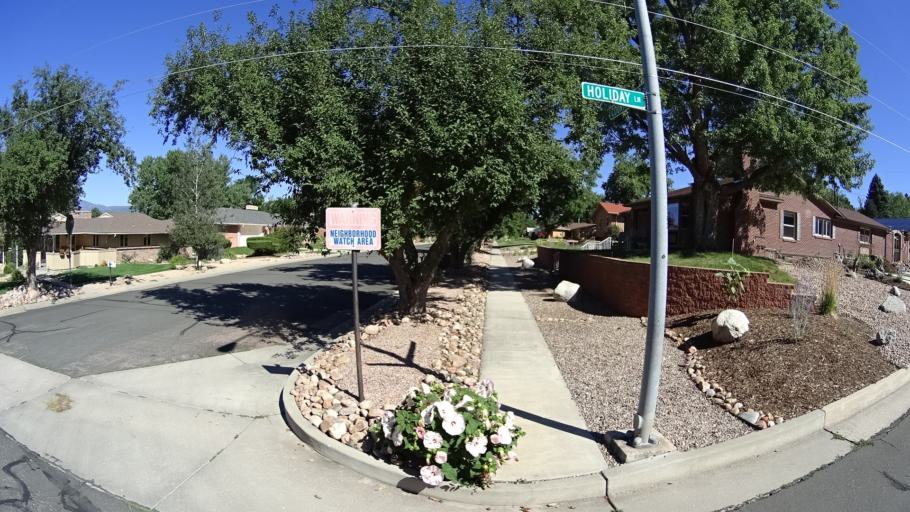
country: US
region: Colorado
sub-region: El Paso County
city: Colorado Springs
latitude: 38.8699
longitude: -104.7809
